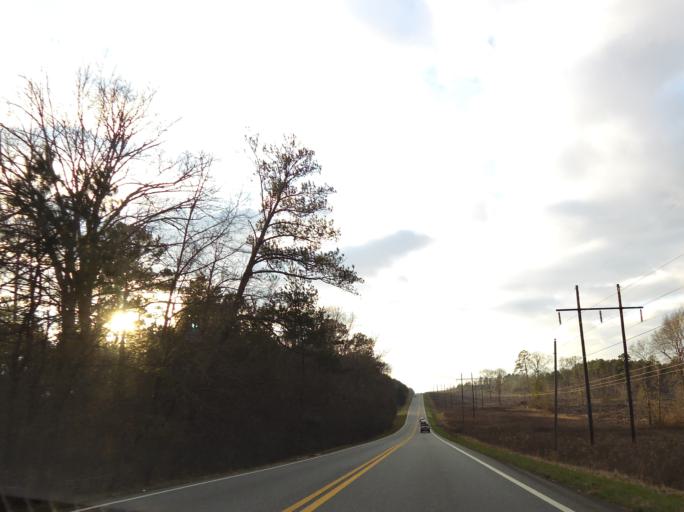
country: US
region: Georgia
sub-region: Houston County
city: Robins Air Force Base
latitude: 32.5404
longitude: -83.4607
